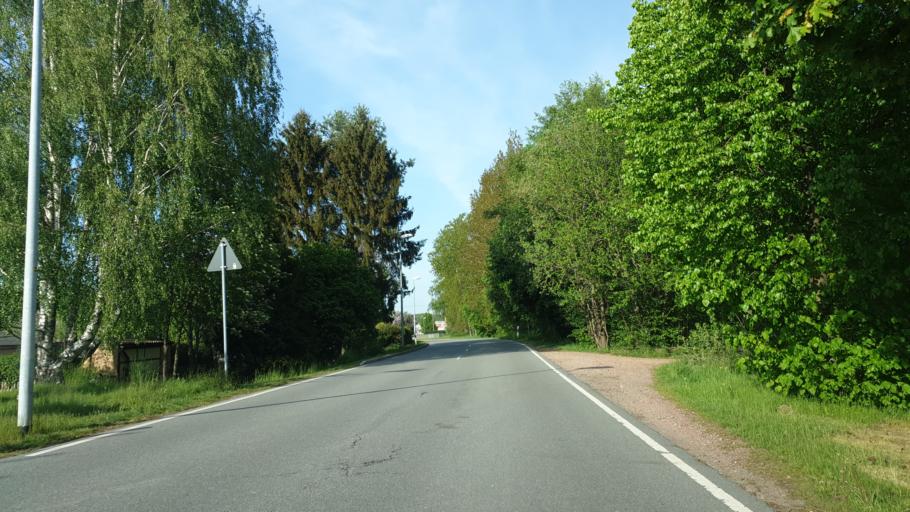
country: DE
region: Saxony
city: Jahnsdorf
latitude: 50.7480
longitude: 12.8250
